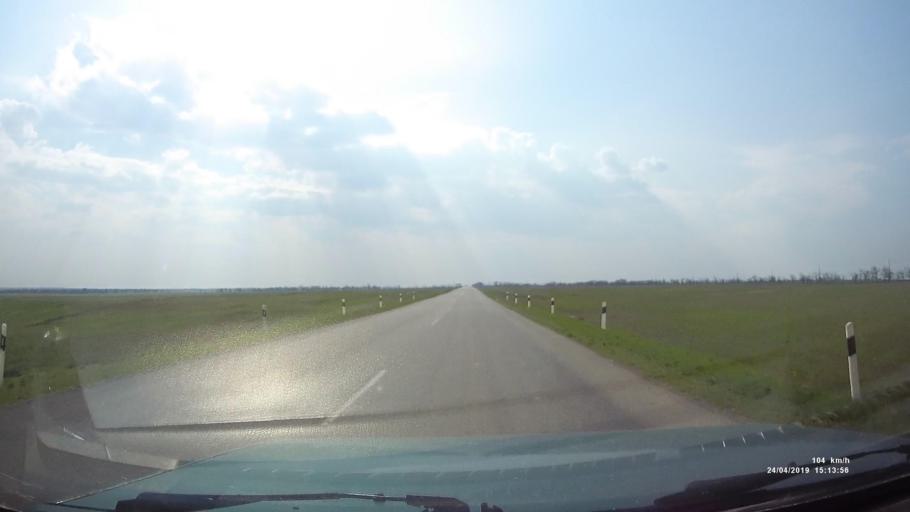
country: RU
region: Rostov
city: Remontnoye
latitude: 46.5465
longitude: 43.2692
